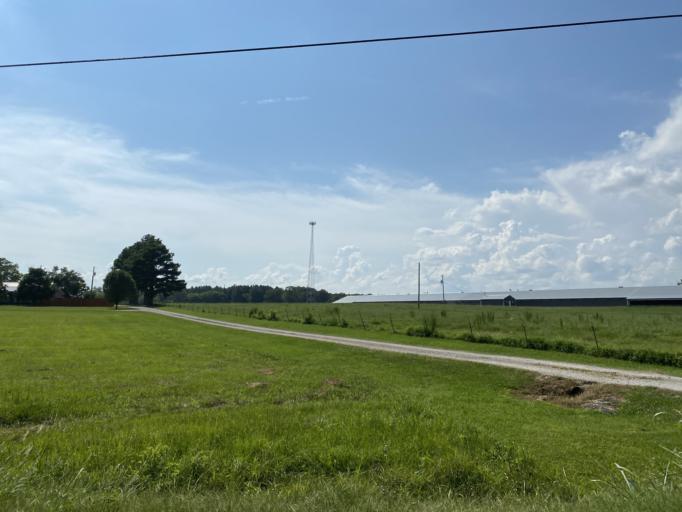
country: US
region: Alabama
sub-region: Lawrence County
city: Town Creek
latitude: 34.6301
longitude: -87.4096
